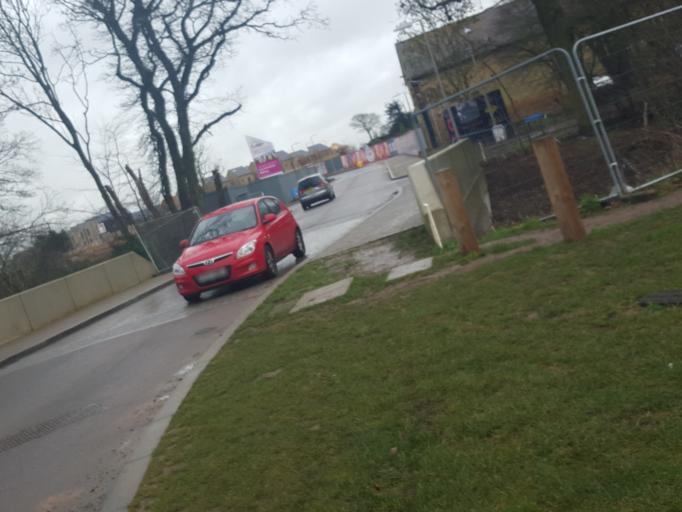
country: GB
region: England
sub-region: Essex
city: Harlow
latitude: 51.7728
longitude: 0.1383
